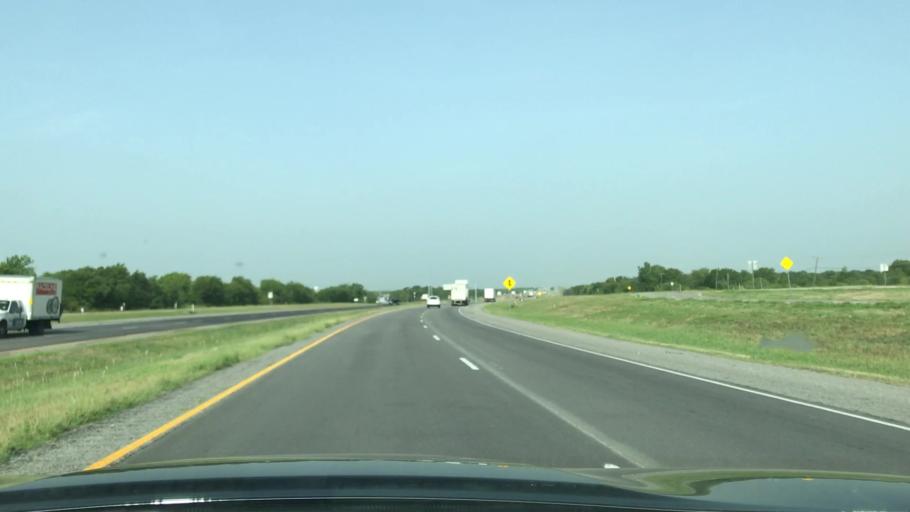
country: US
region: Texas
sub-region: Kaufman County
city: Talty
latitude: 32.7396
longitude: -96.3682
